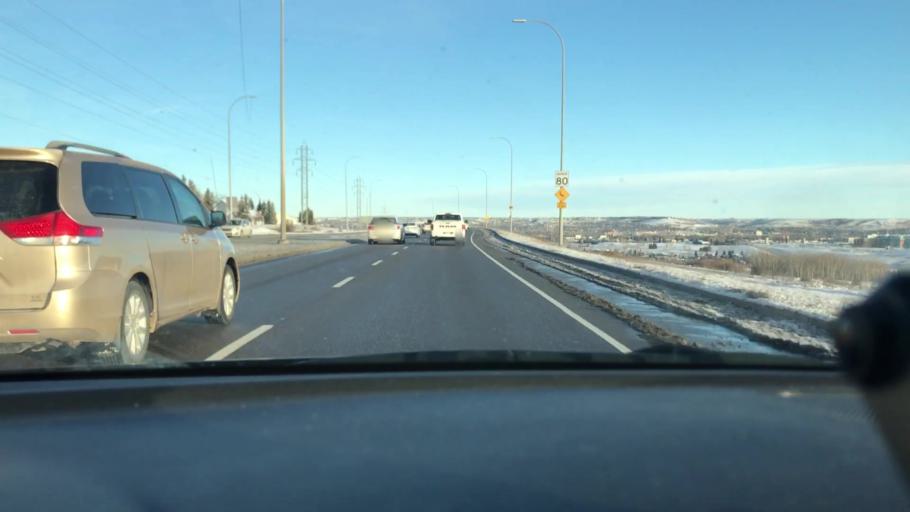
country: CA
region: Alberta
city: Calgary
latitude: 51.0555
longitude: -114.1649
